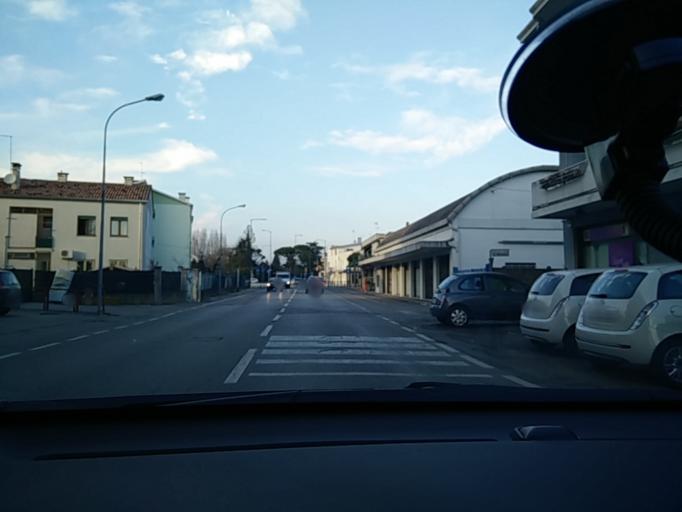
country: IT
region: Veneto
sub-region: Provincia di Venezia
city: San Dona di Piave
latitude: 45.6299
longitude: 12.5855
